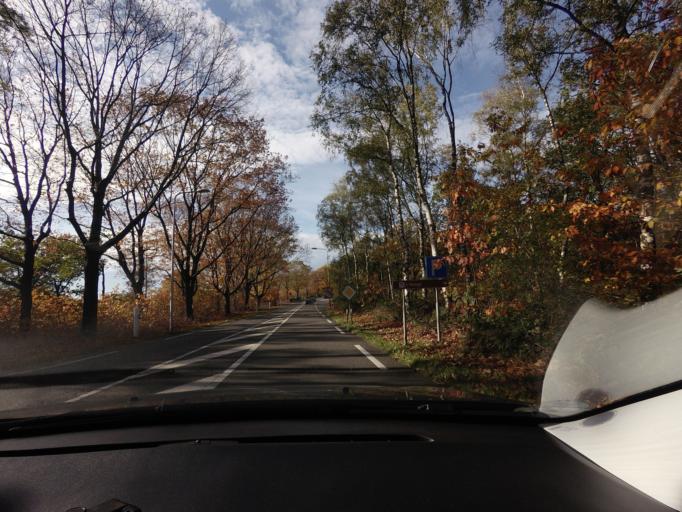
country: NL
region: Utrecht
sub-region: Gemeente Soest
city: Soest
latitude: 52.1316
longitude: 5.2933
